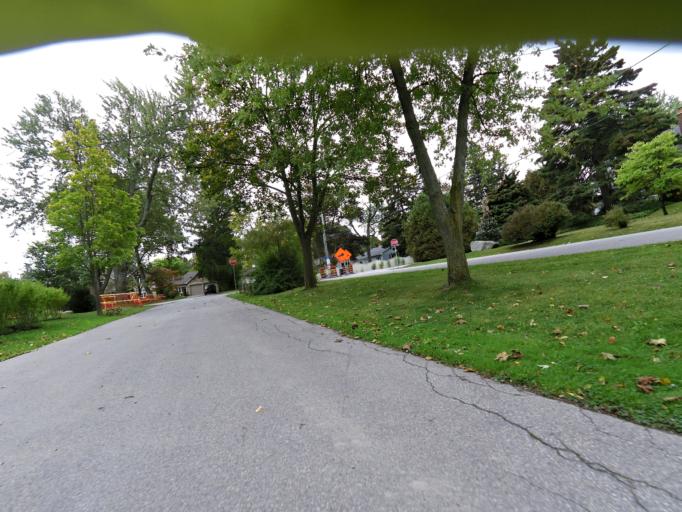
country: CA
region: Ontario
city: Scarborough
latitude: 43.7271
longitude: -79.2252
